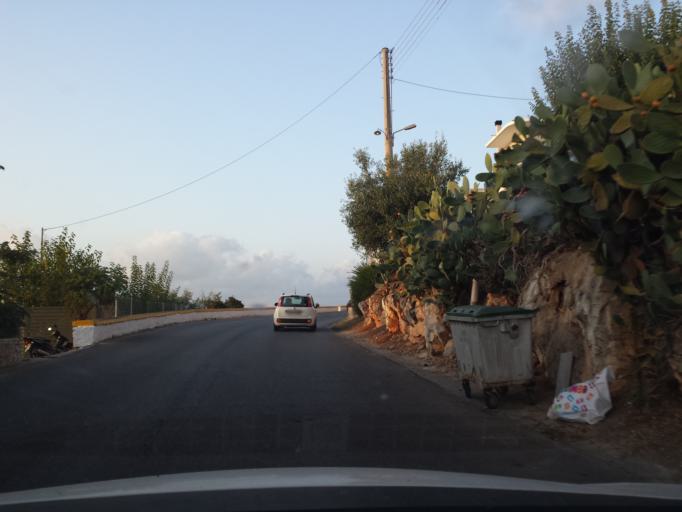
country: GR
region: Peloponnese
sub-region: Nomos Messinias
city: Pylos
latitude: 36.9181
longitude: 21.7018
